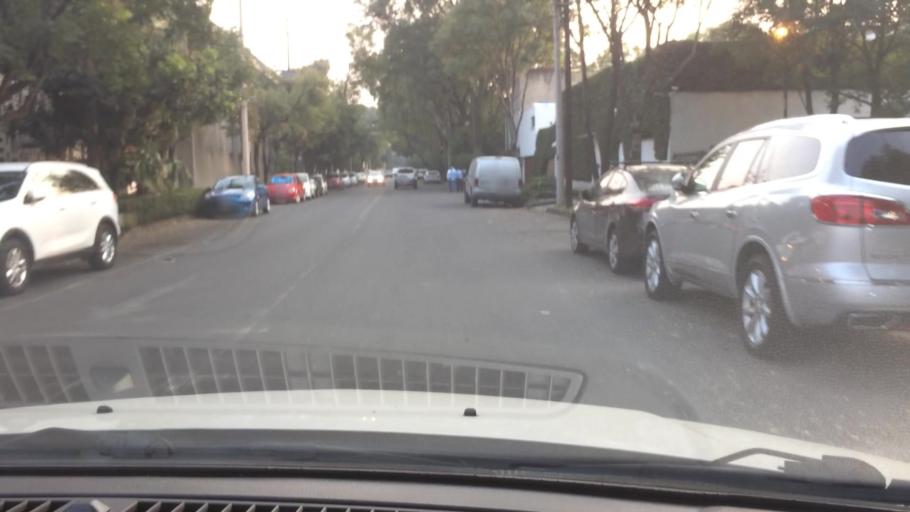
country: MX
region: Mexico City
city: Alvaro Obregon
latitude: 19.3560
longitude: -99.1910
